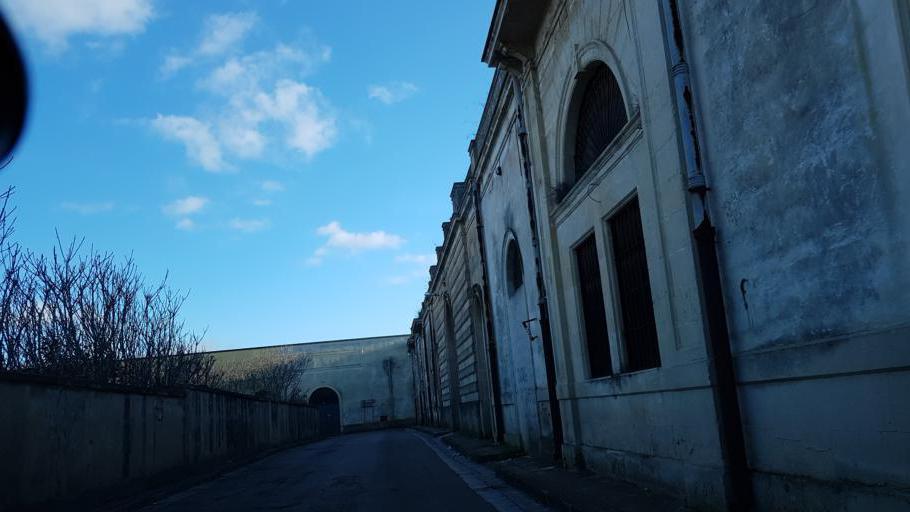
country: IT
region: Apulia
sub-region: Provincia di Lecce
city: Squinzano
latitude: 40.4402
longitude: 18.0438
